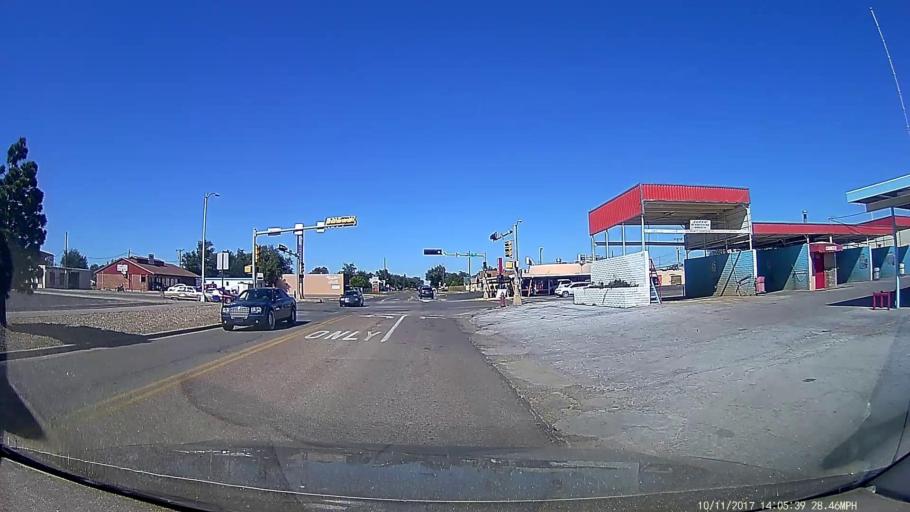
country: US
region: New Mexico
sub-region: Curry County
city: Clovis
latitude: 34.4044
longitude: -103.2142
